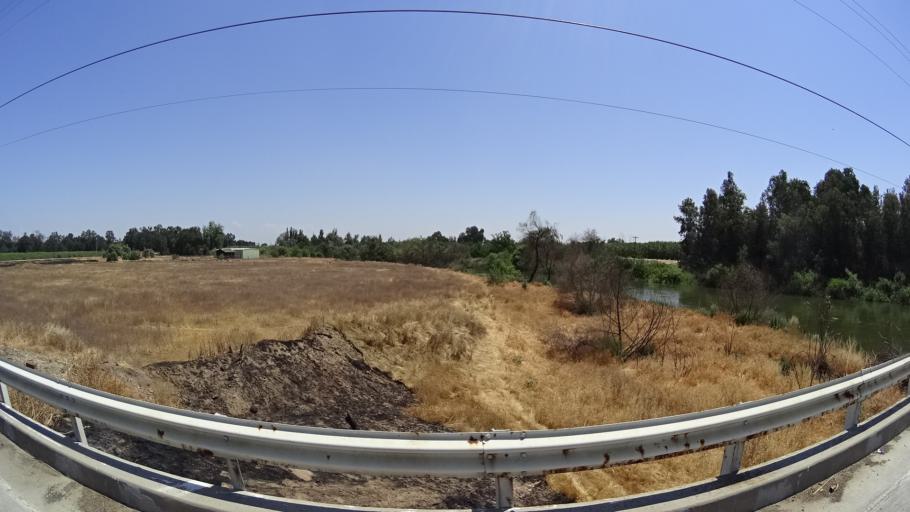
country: US
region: California
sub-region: Fresno County
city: Laton
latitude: 36.4267
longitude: -119.6862
